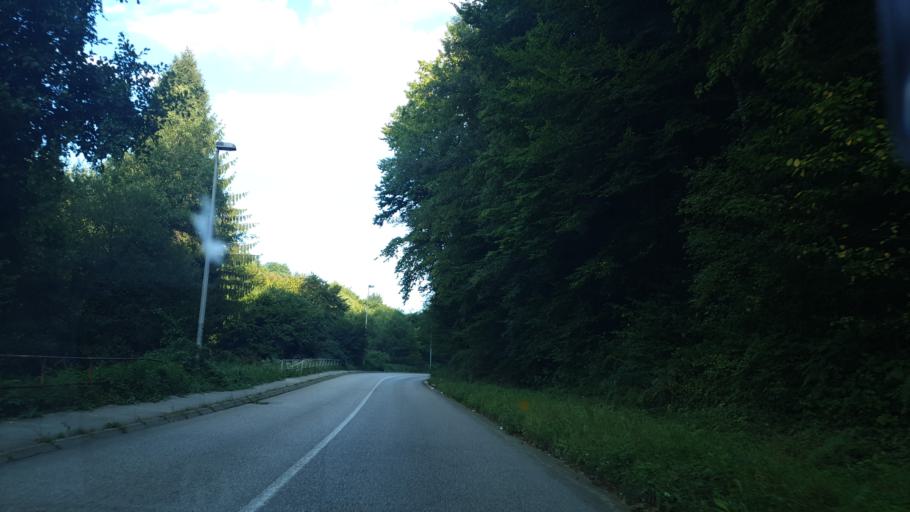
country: RS
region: Central Serbia
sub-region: Zlatiborski Okrug
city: Uzice
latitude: 43.8594
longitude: 19.8619
